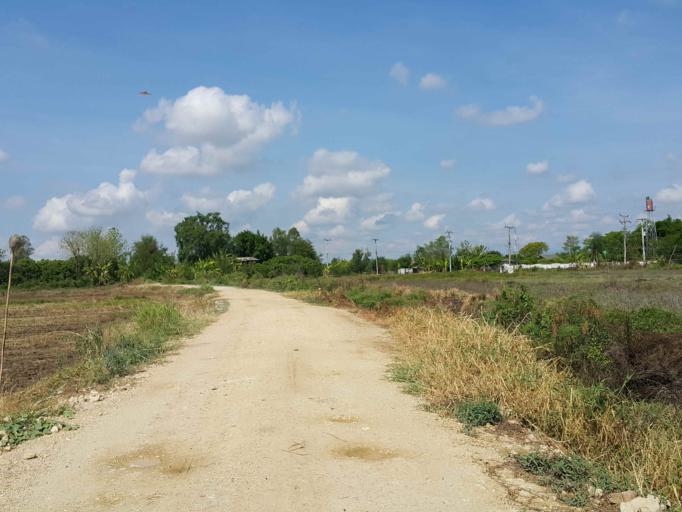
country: TH
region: Chiang Mai
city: San Kamphaeng
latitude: 18.7239
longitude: 99.0847
